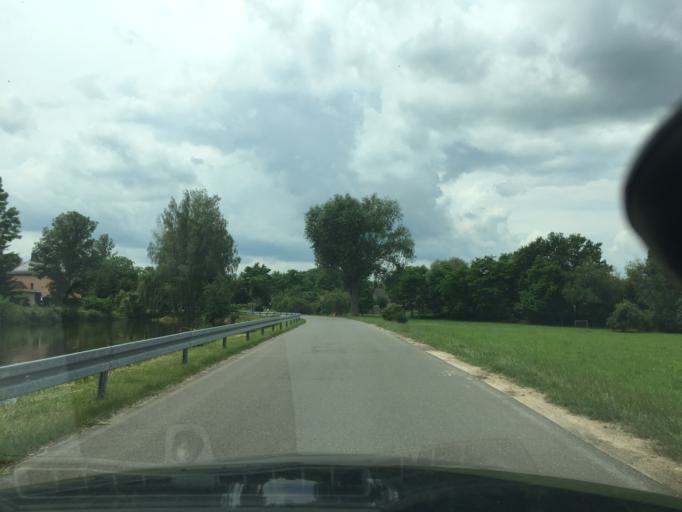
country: DE
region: Thuringia
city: Vollmershain
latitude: 50.8674
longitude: 12.3231
